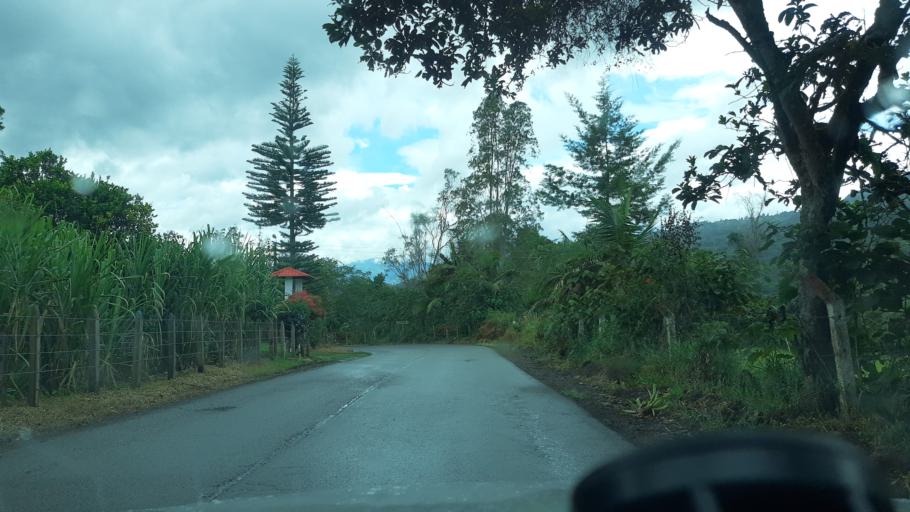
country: CO
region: Boyaca
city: Chinavita
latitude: 5.1434
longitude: -73.3657
